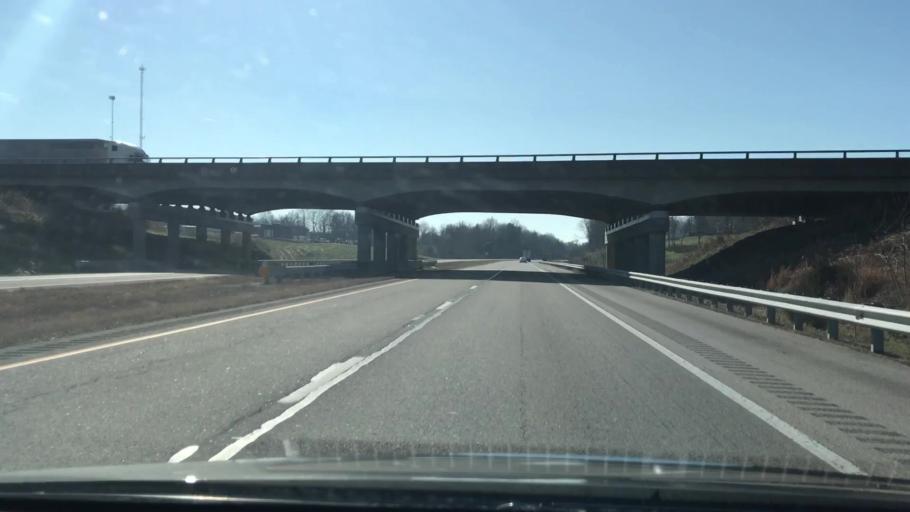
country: US
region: Kentucky
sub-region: Barren County
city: Glasgow
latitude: 36.9849
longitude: -85.8956
